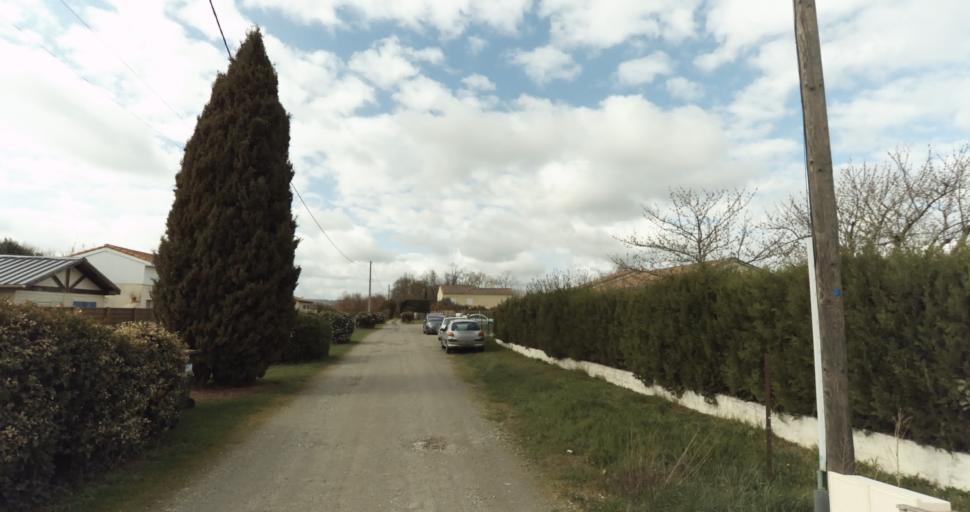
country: FR
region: Midi-Pyrenees
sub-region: Departement de la Haute-Garonne
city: Auterive
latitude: 43.3551
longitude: 1.4611
